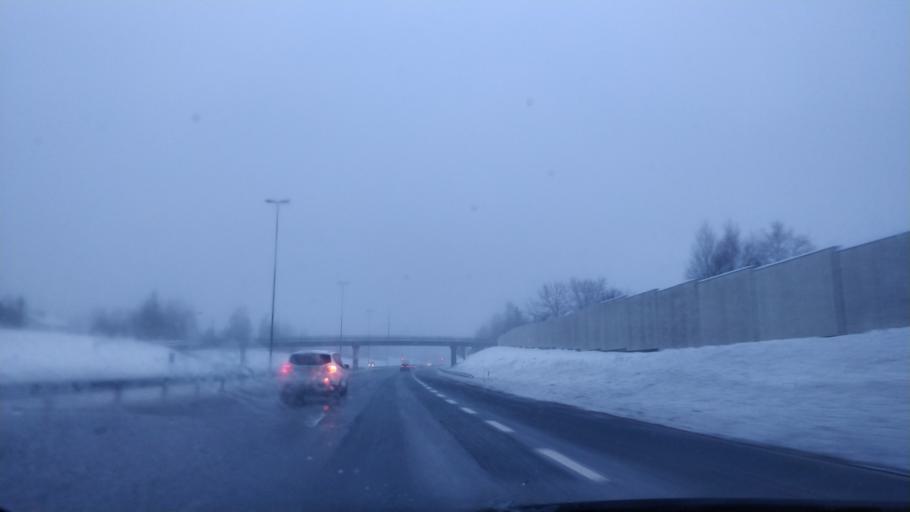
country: FI
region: Lapland
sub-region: Kemi-Tornio
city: Kemi
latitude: 65.7456
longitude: 24.5810
